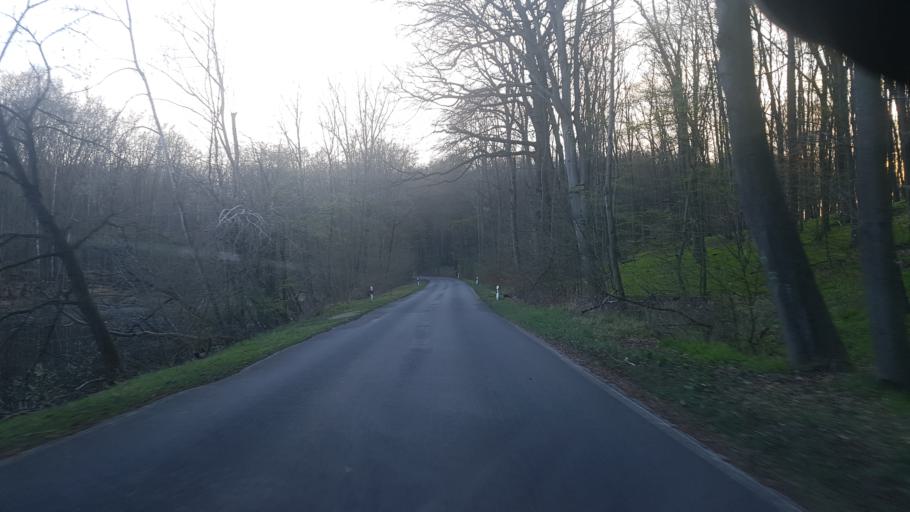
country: DE
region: Brandenburg
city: Gramzow
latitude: 53.1825
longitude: 13.9104
